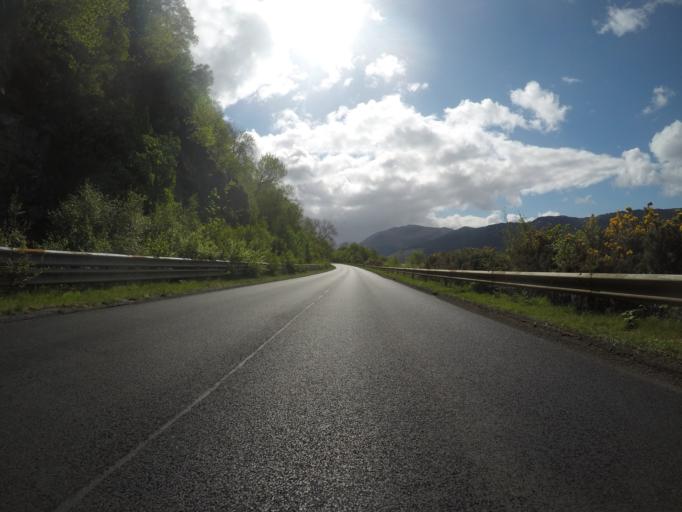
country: GB
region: Scotland
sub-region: Highland
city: Fort William
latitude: 57.2526
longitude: -5.4751
